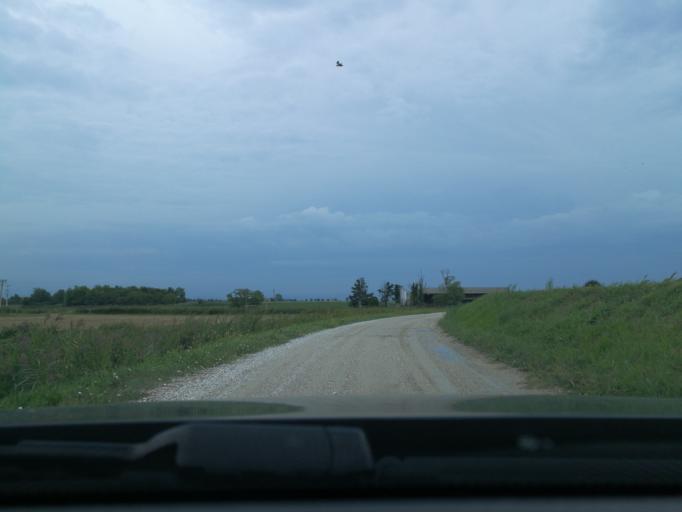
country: IT
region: Friuli Venezia Giulia
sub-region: Provincia di Udine
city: Pertegada
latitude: 45.7173
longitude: 13.0682
